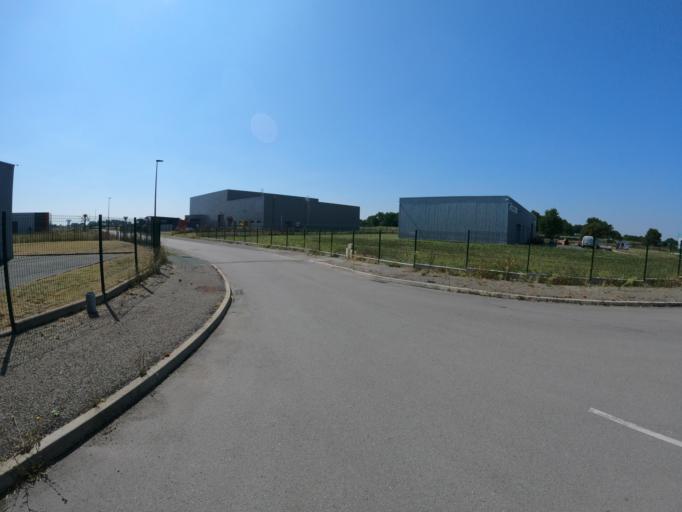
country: FR
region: Pays de la Loire
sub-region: Departement de la Loire-Atlantique
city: Geneston
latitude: 47.0662
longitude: -1.5047
